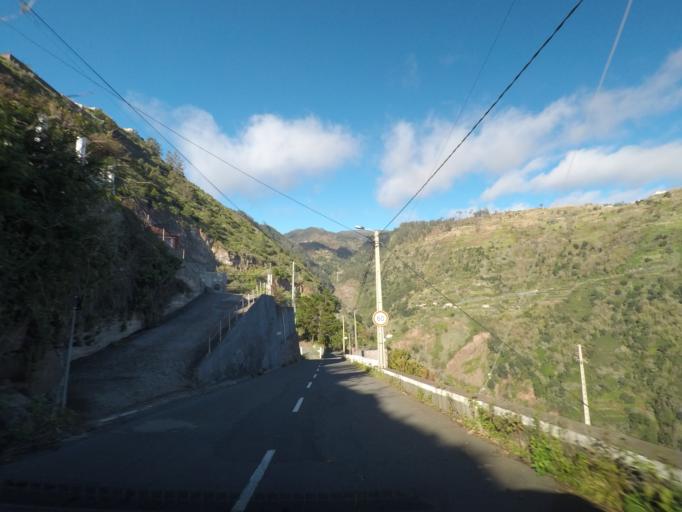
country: PT
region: Madeira
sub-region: Calheta
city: Arco da Calheta
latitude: 32.7086
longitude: -17.1373
